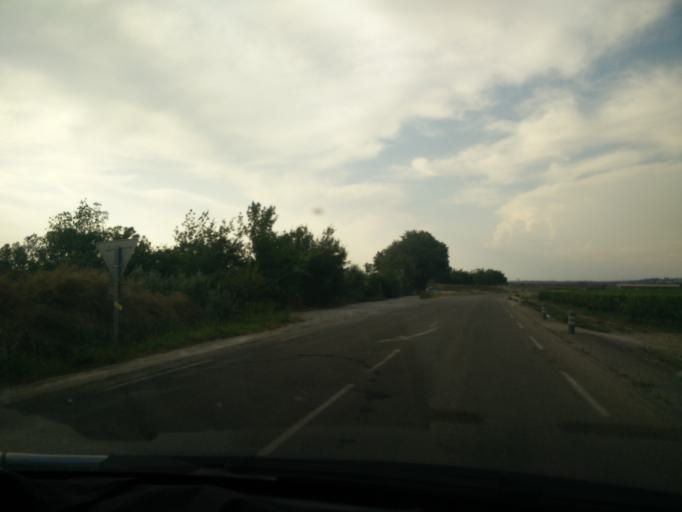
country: FR
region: Languedoc-Roussillon
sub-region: Departement du Gard
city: Gallargues-le-Montueux
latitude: 43.6959
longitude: 4.1676
